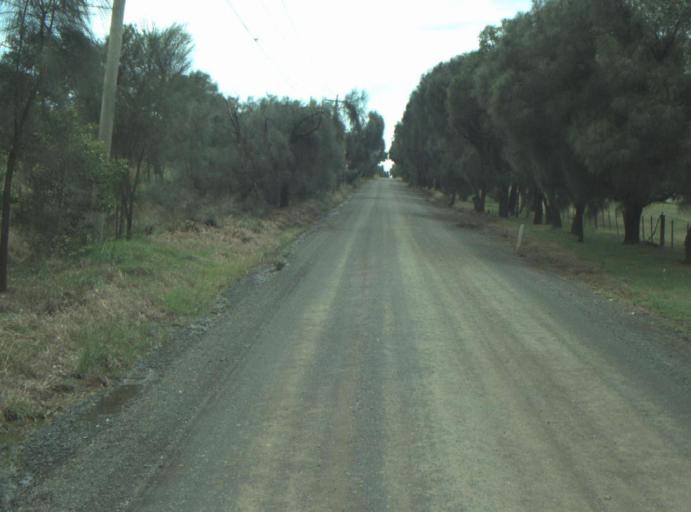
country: AU
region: Victoria
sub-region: Greater Geelong
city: Clifton Springs
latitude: -38.2129
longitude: 144.5630
